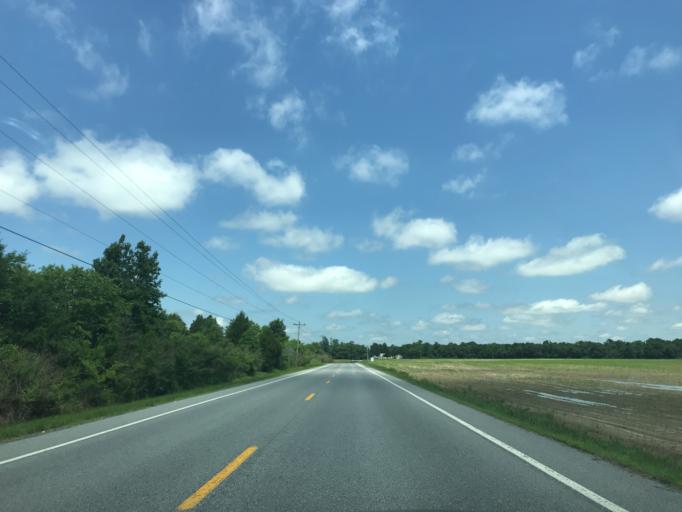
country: US
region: Maryland
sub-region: Caroline County
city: Federalsburg
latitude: 38.7256
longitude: -75.7335
